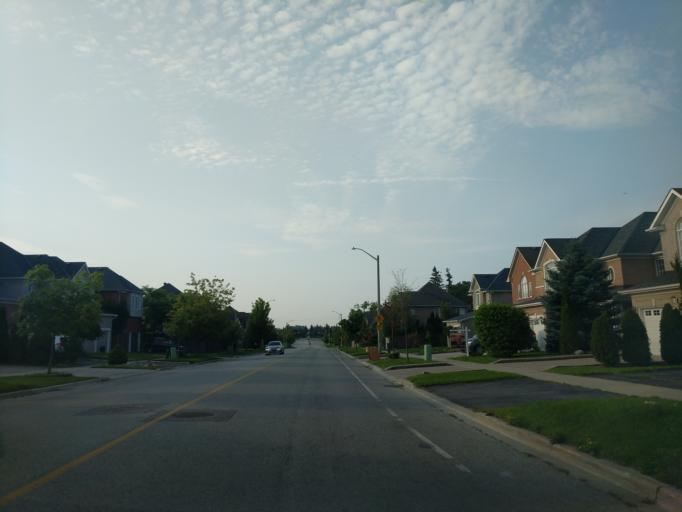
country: CA
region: Ontario
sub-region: York
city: Richmond Hill
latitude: 43.8804
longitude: -79.4079
